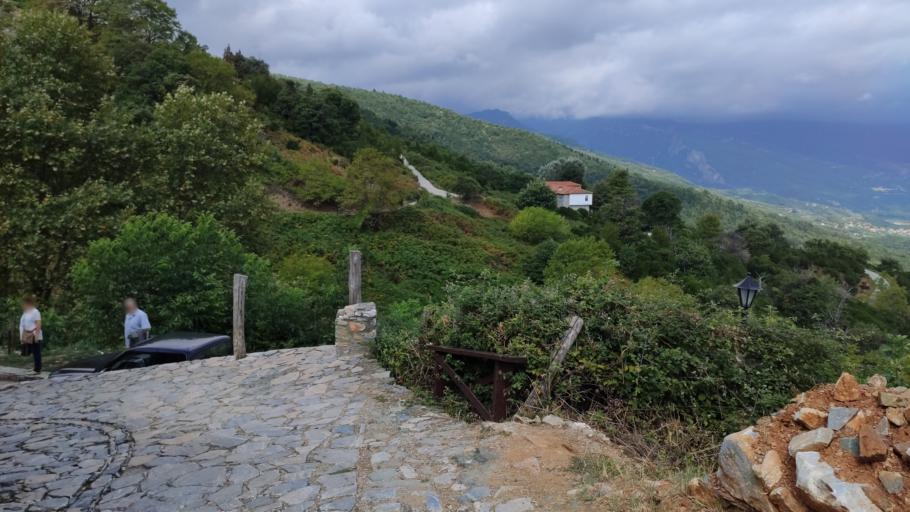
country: GR
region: Central Macedonia
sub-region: Nomos Pierias
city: Leptokarya
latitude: 39.9921
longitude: 22.5701
